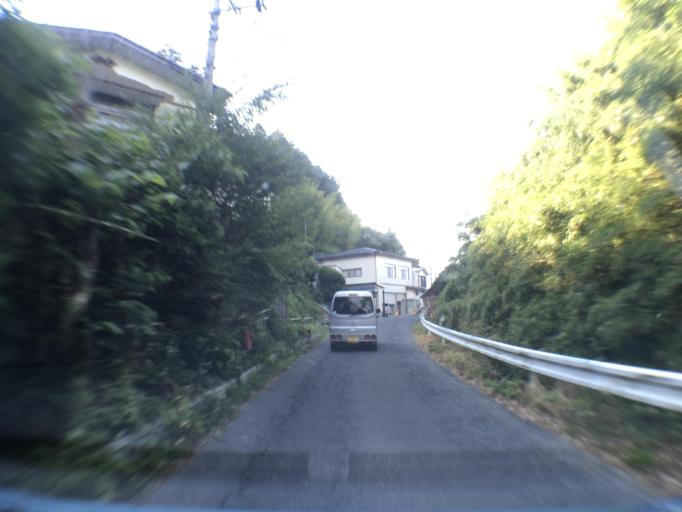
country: JP
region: Miyagi
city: Wakuya
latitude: 38.6464
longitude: 141.2818
